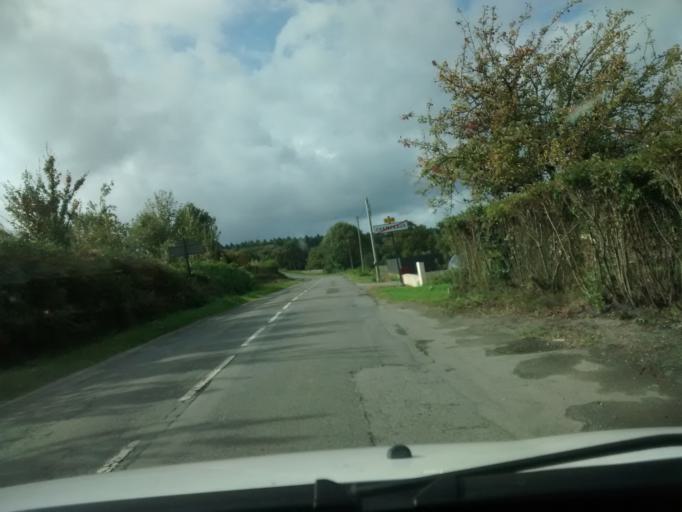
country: FR
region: Brittany
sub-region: Departement d'Ille-et-Vilaine
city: Poce-les-Bois
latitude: 48.1484
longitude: -1.3148
